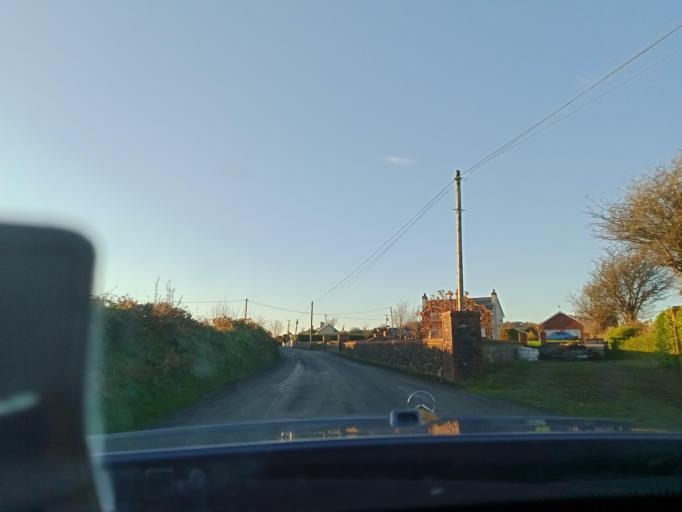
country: IE
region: Leinster
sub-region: Loch Garman
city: New Ross
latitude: 52.3701
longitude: -7.0330
